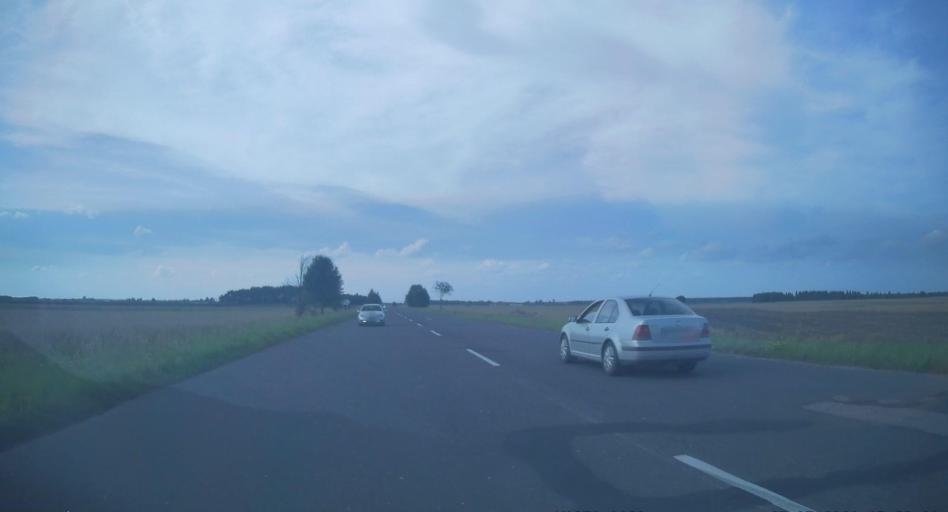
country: PL
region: Lodz Voivodeship
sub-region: Powiat tomaszowski
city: Rzeczyca
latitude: 51.6564
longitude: 20.2740
